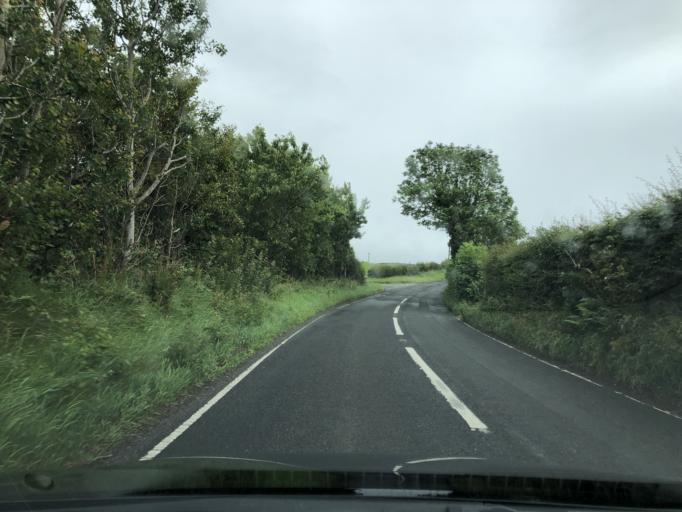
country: GB
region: Northern Ireland
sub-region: Down District
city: Dundrum
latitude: 54.2775
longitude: -5.8004
